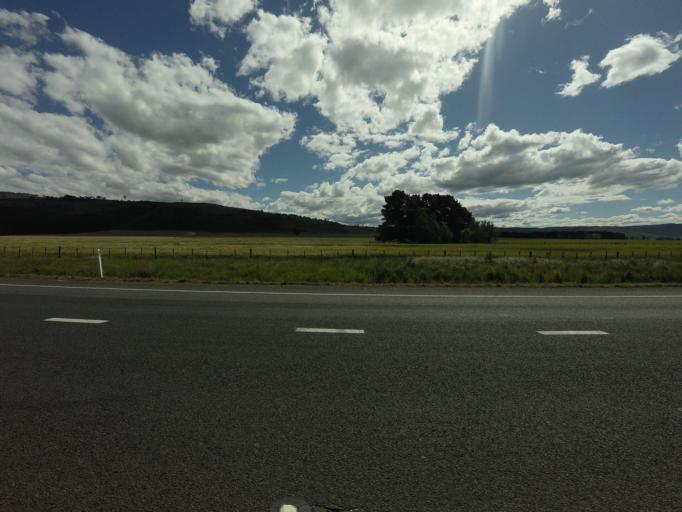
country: AU
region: Tasmania
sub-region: Northern Midlands
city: Evandale
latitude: -42.0389
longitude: 147.4832
